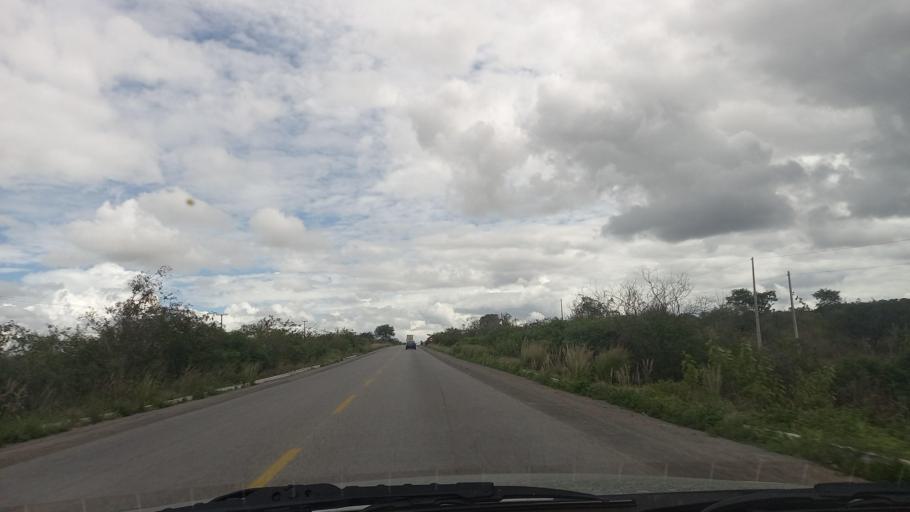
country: BR
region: Pernambuco
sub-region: Cachoeirinha
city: Cachoeirinha
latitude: -8.3423
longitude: -36.1619
